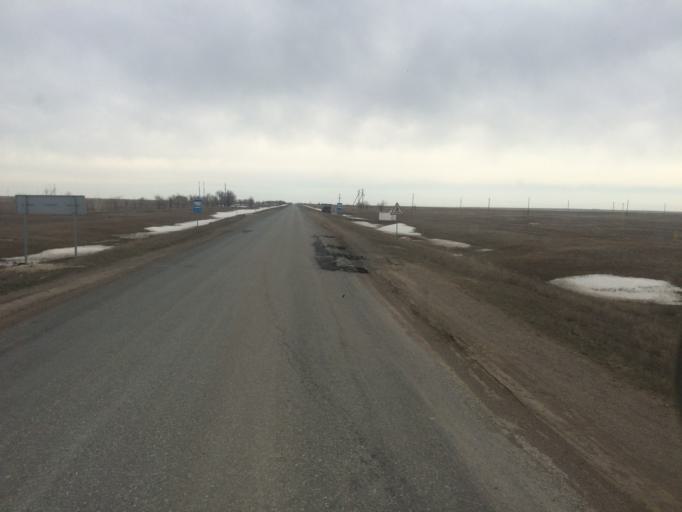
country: KZ
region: Batys Qazaqstan
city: Fedorovka
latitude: 50.6508
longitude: 52.0880
